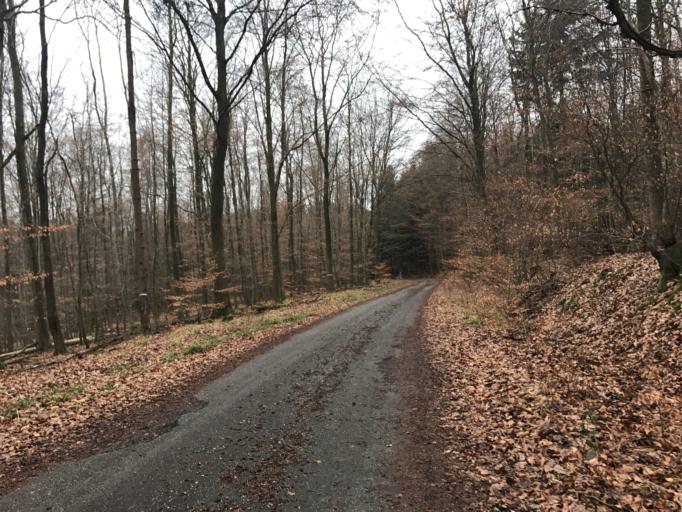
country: DE
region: Hesse
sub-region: Regierungsbezirk Darmstadt
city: Wiesbaden
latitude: 50.1313
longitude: 8.2308
